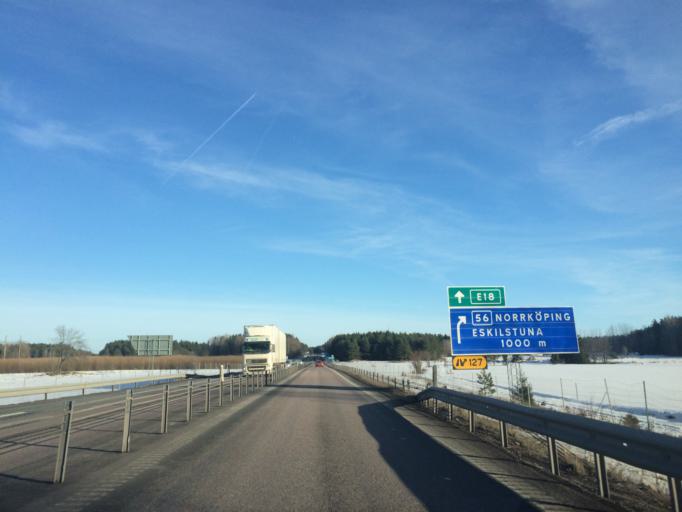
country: SE
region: Vaestmanland
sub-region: Hallstahammars Kommun
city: Kolback
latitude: 59.5791
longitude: 16.3257
